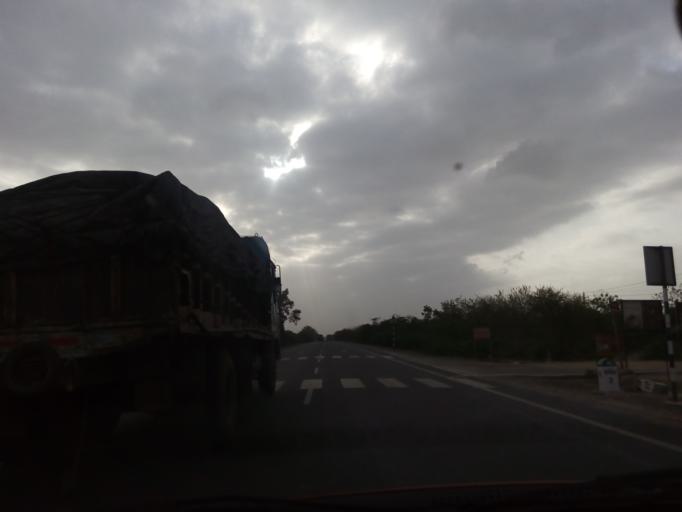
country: IN
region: Gujarat
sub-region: Kachchh
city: Bhuj
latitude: 23.2377
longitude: 69.7968
